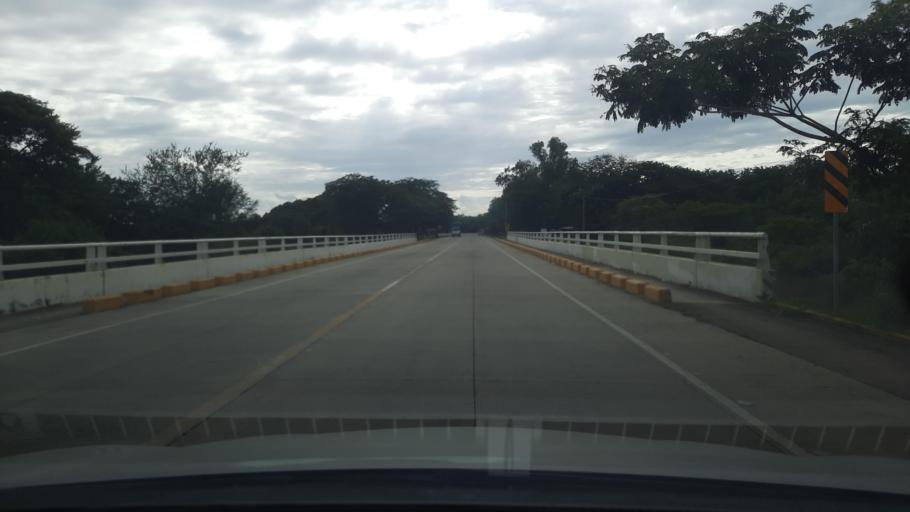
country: NI
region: Chinandega
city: Somotillo
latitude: 12.8602
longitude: -86.8605
